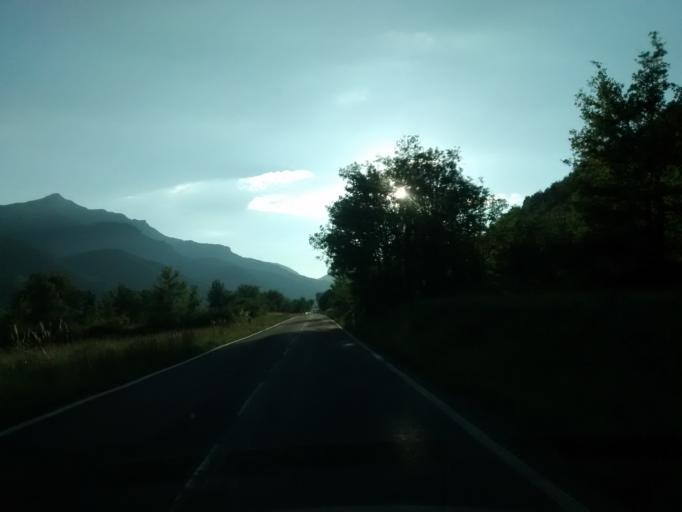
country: ES
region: Aragon
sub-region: Provincia de Huesca
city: Fiscal
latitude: 42.4757
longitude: -0.0558
